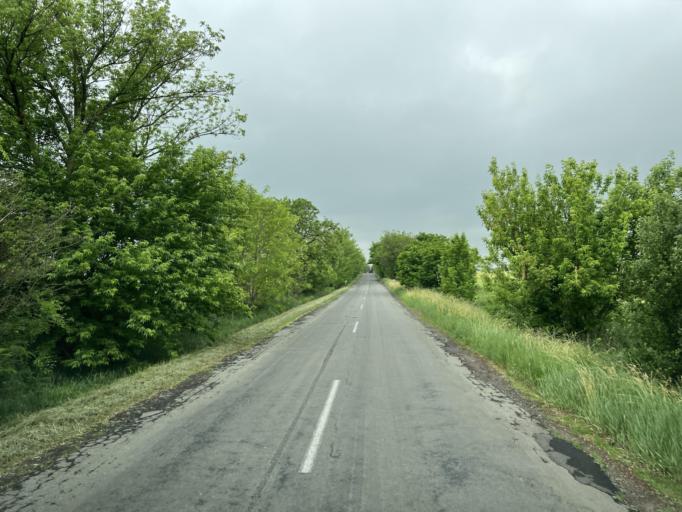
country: HU
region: Pest
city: Tura
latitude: 47.6179
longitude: 19.6378
